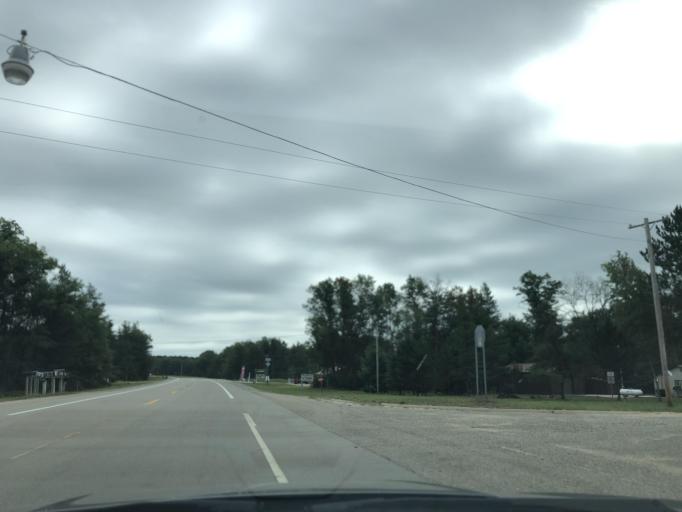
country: US
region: Michigan
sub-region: Clare County
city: Harrison
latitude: 44.0330
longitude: -85.0246
